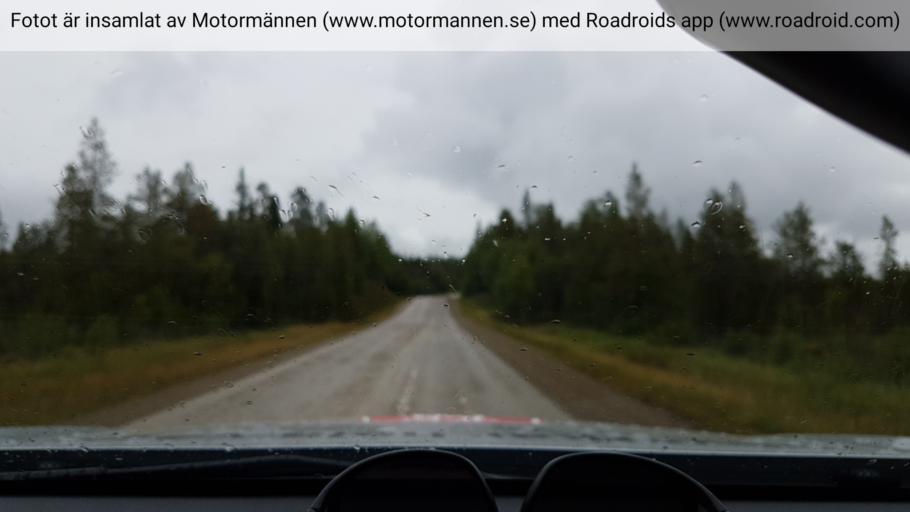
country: SE
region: Vaesterbotten
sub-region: Asele Kommun
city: Insjon
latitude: 64.8005
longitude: 17.5948
